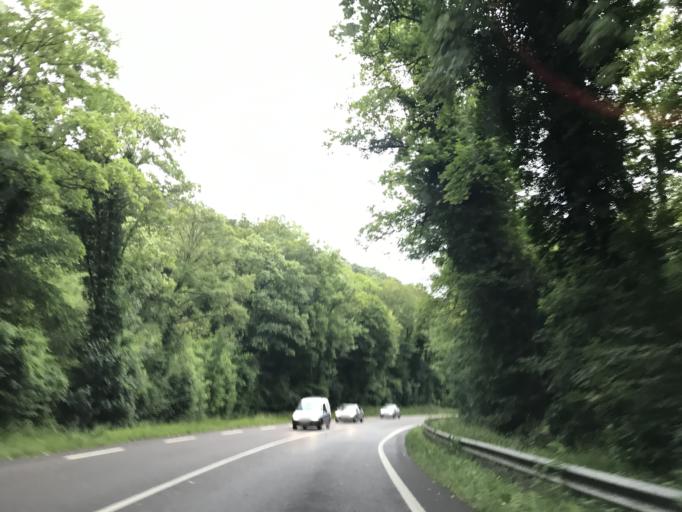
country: FR
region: Ile-de-France
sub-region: Departement des Yvelines
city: Bennecourt
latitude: 49.0283
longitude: 1.5465
